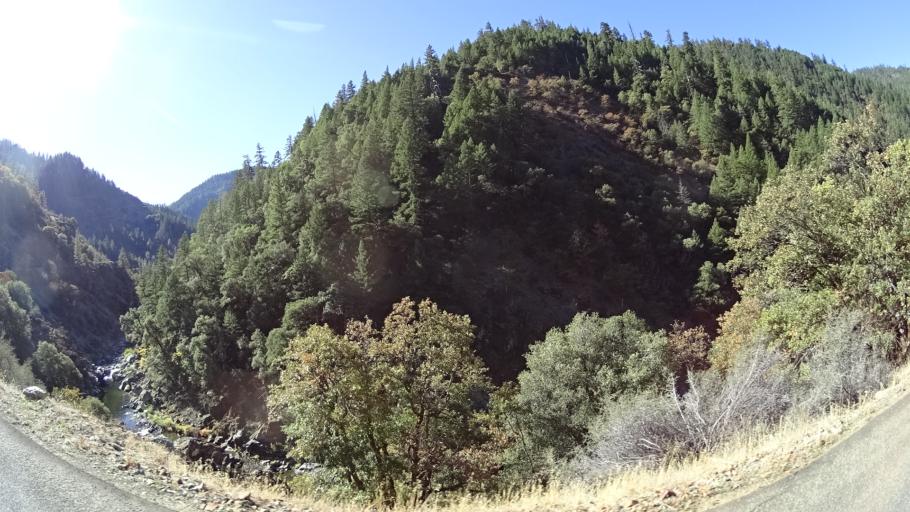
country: US
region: California
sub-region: Humboldt County
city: Willow Creek
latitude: 41.1642
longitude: -123.2093
